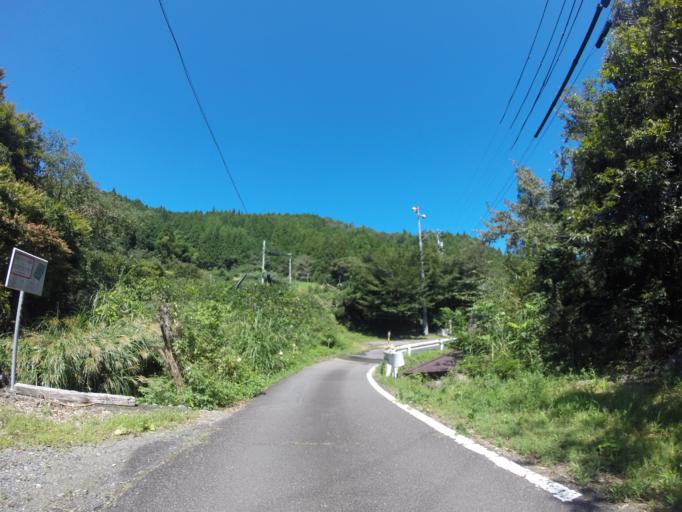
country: JP
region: Shizuoka
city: Fujieda
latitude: 34.9526
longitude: 138.1663
